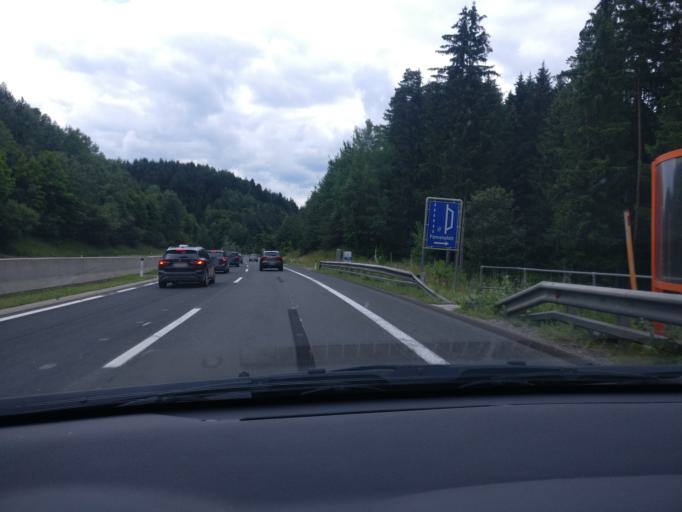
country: AT
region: Lower Austria
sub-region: Politischer Bezirk Neunkirchen
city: Thomasberg
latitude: 47.5488
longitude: 16.1323
